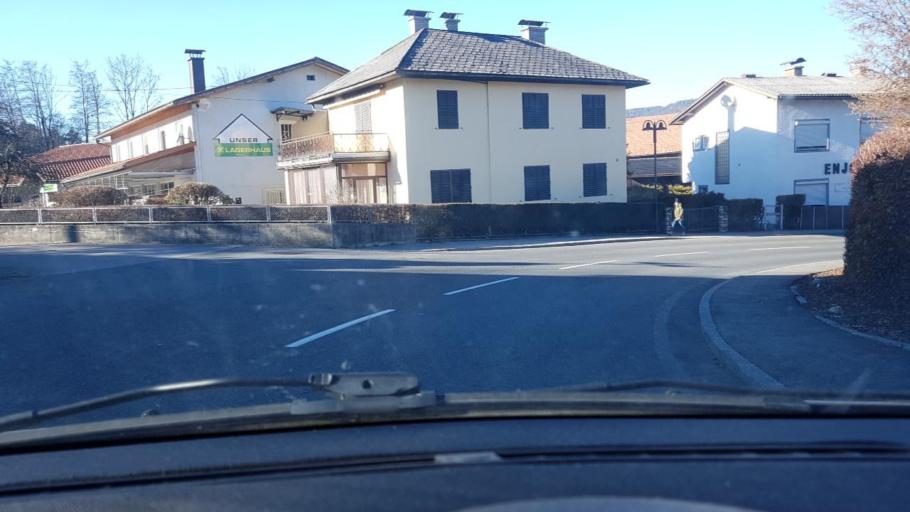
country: AT
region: Carinthia
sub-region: Politischer Bezirk Villach Land
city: Velden am Woerthersee
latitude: 46.6095
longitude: 14.0394
